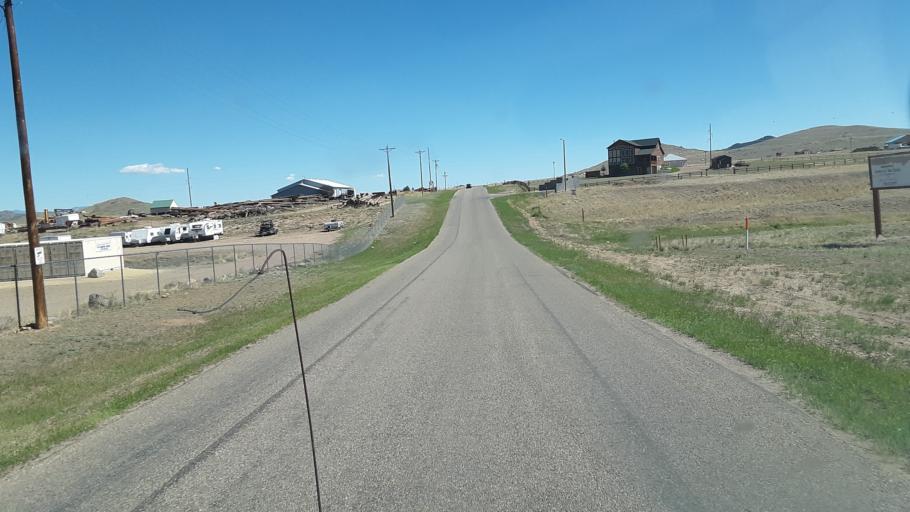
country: US
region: Colorado
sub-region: Custer County
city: Westcliffe
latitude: 38.1428
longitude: -105.4681
